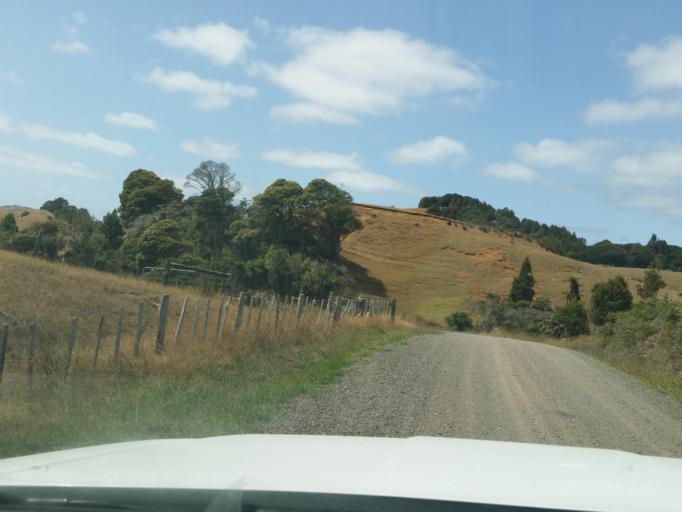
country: NZ
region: Northland
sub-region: Far North District
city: Waimate North
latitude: -35.6183
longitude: 173.7137
